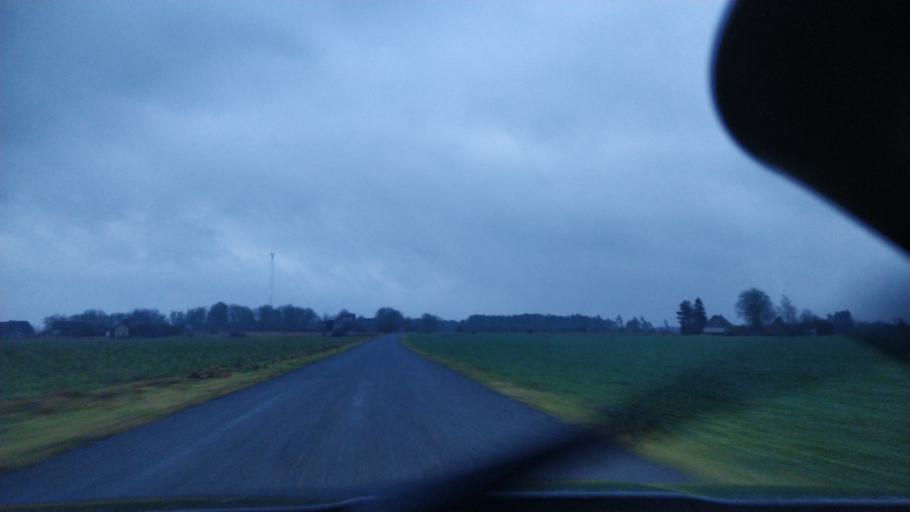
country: EE
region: Laeaene
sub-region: Lihula vald
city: Lihula
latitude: 58.8443
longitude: 24.0320
